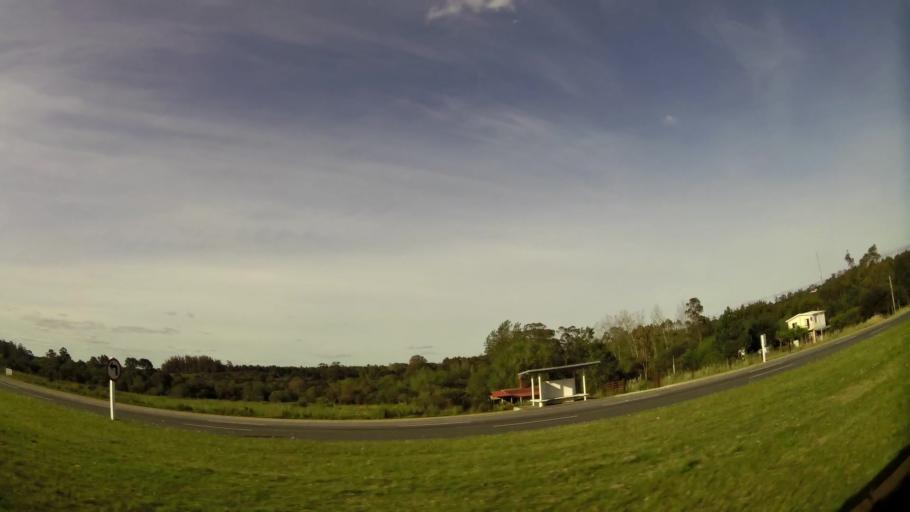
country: UY
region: Canelones
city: La Floresta
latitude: -34.7773
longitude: -55.5612
